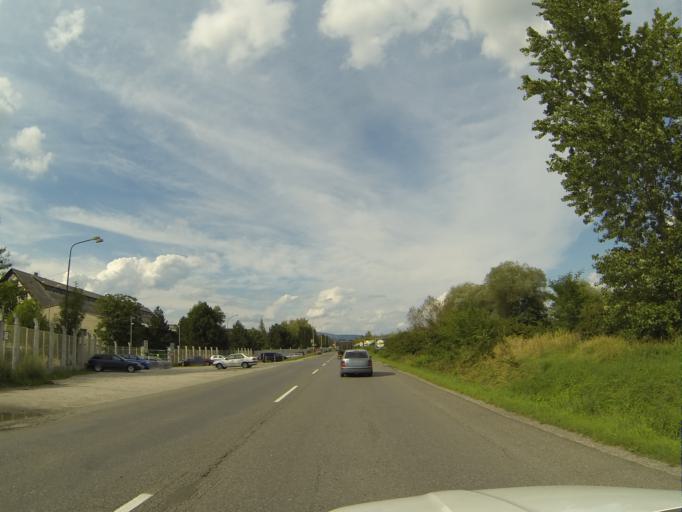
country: SK
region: Nitriansky
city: Novaky
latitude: 48.7043
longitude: 18.5364
